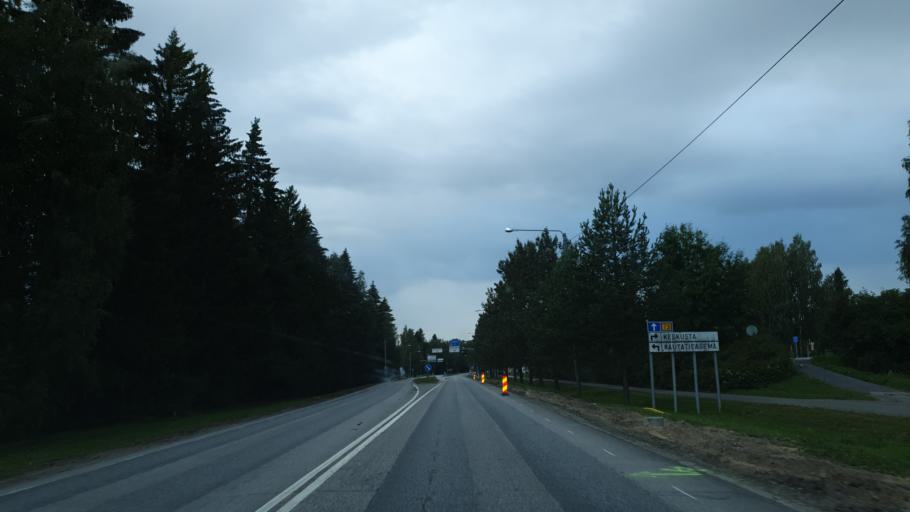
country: FI
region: North Karelia
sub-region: Pielisen Karjala
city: Lieksa
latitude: 63.3175
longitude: 30.0222
